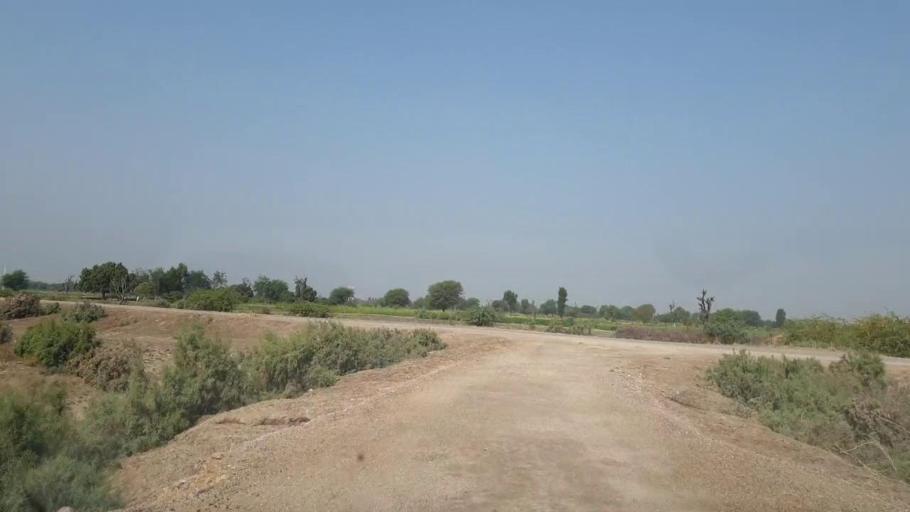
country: PK
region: Sindh
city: Mirpur Khas
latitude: 25.6219
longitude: 69.1024
